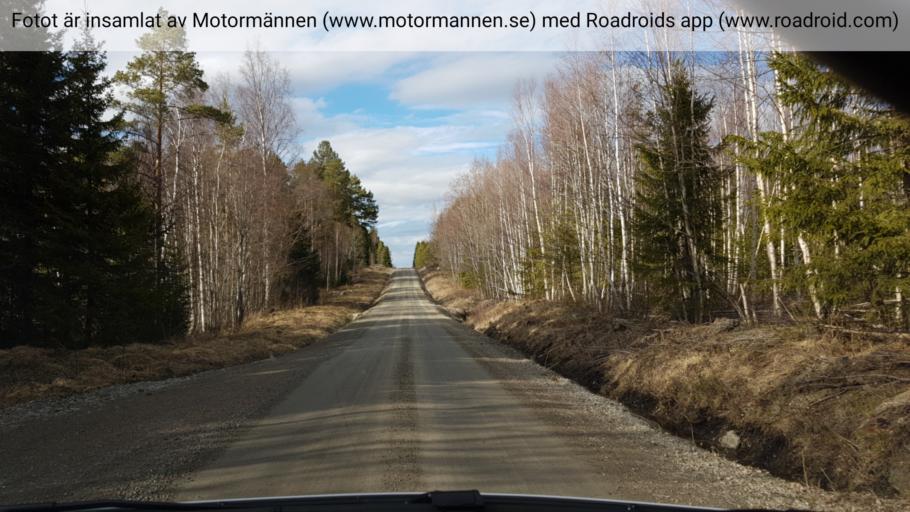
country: SE
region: Jaemtland
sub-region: Bergs Kommun
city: Hoverberg
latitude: 62.8220
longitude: 14.6635
